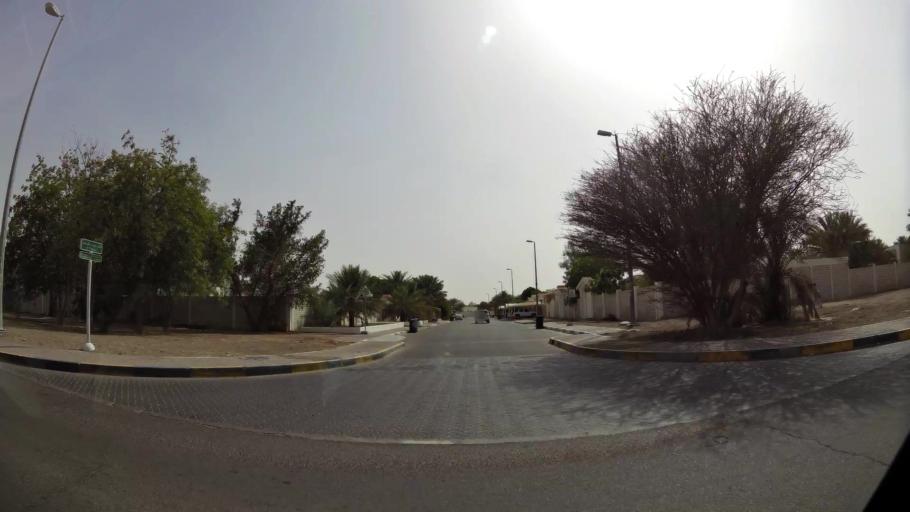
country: AE
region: Abu Dhabi
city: Al Ain
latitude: 24.1797
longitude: 55.6097
